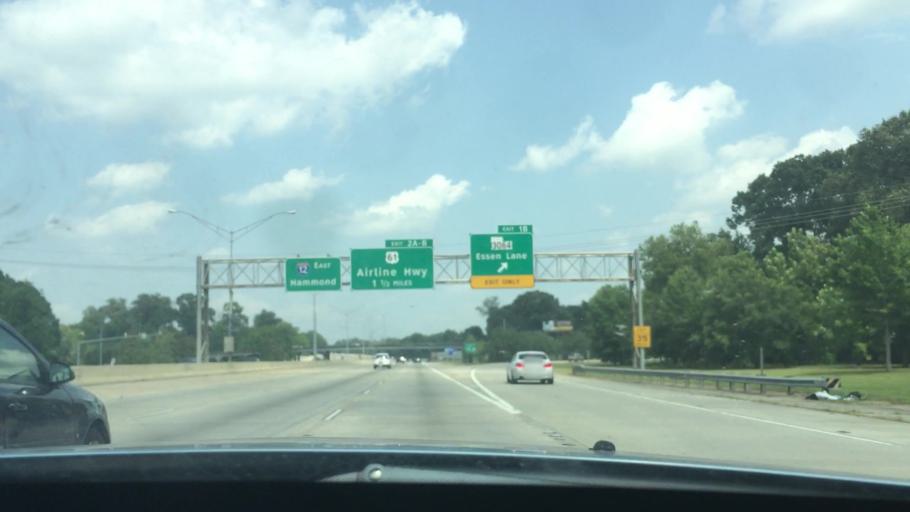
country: US
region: Louisiana
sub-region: East Baton Rouge Parish
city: Westminster
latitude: 30.4174
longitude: -91.1016
